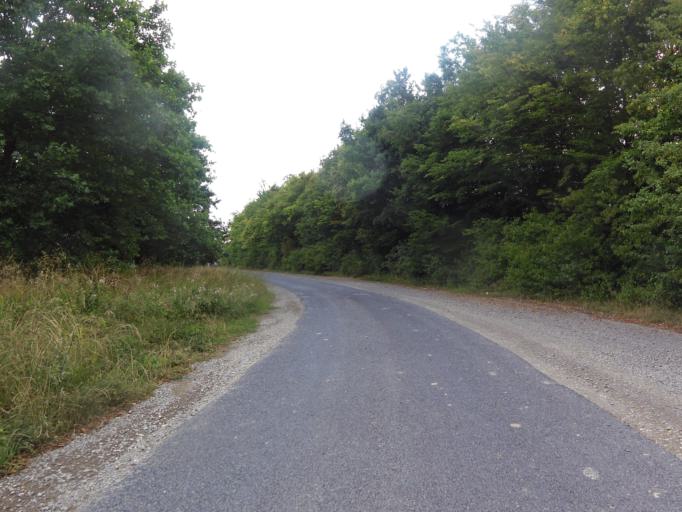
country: DE
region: Bavaria
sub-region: Regierungsbezirk Unterfranken
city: Randersacker
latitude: 49.7535
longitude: 9.9565
